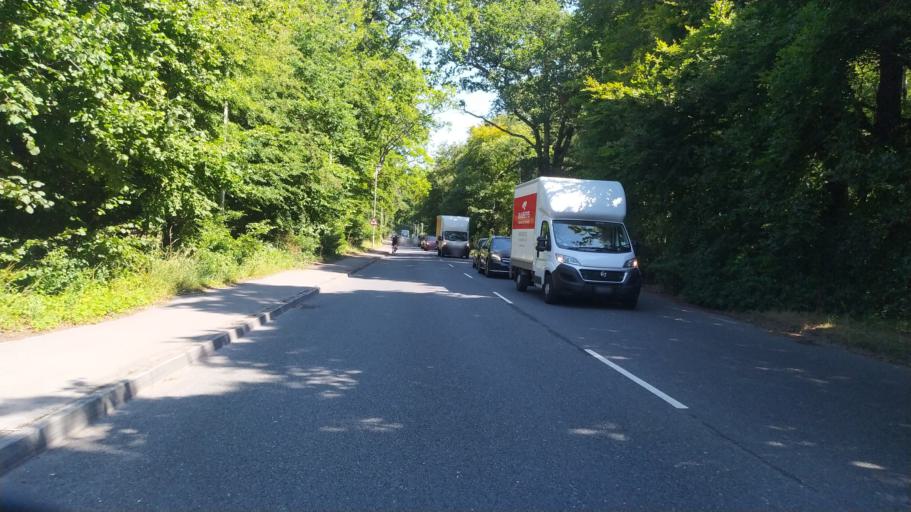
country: GB
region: England
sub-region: Dorset
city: Wareham
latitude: 50.7116
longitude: -2.0944
